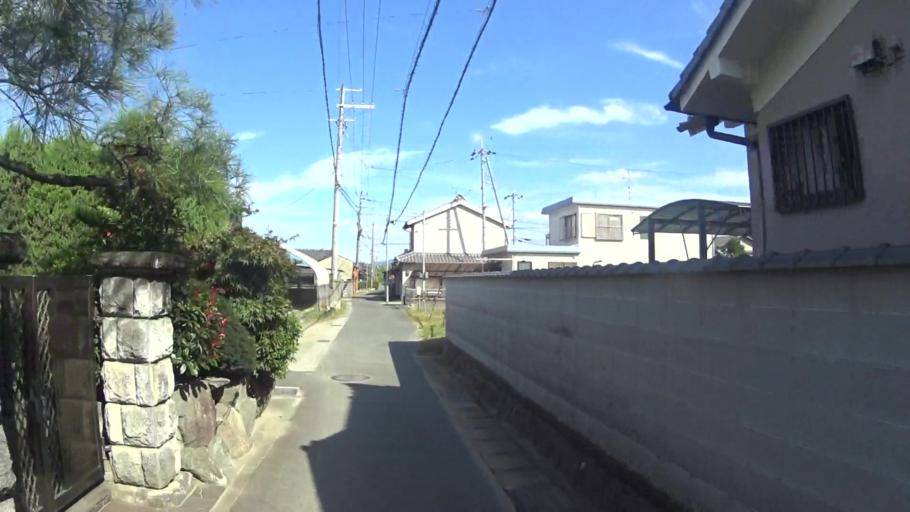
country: JP
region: Kyoto
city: Tanabe
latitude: 34.8547
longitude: 135.7464
